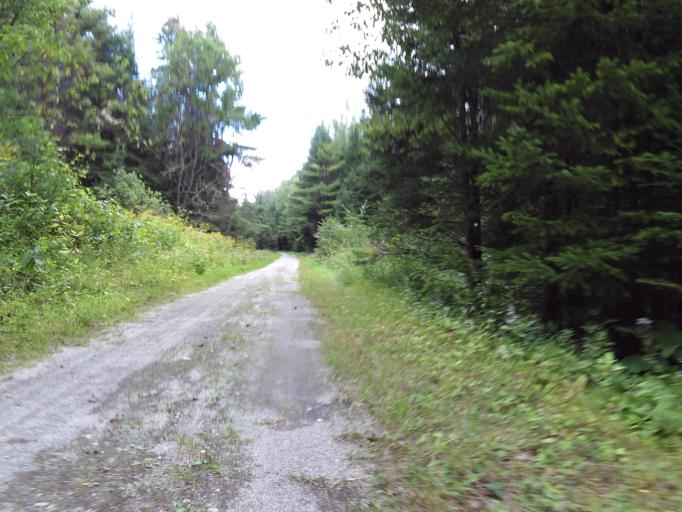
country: CA
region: Quebec
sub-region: Outaouais
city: Wakefield
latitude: 45.8549
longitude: -75.9921
